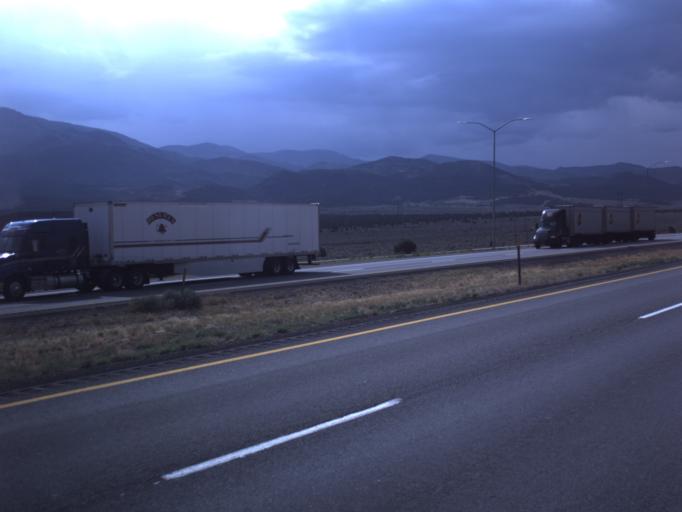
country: US
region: Utah
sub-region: Beaver County
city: Beaver
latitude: 38.5758
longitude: -112.6036
